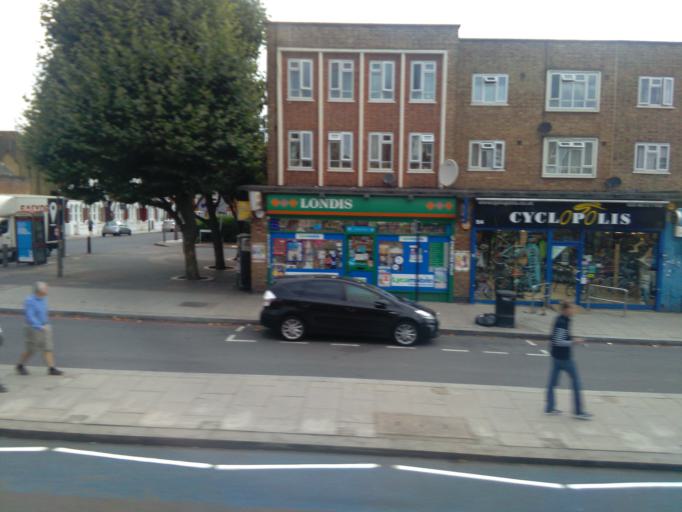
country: GB
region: England
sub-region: Greater London
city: Brixton Hill
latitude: 51.4470
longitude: -0.1493
